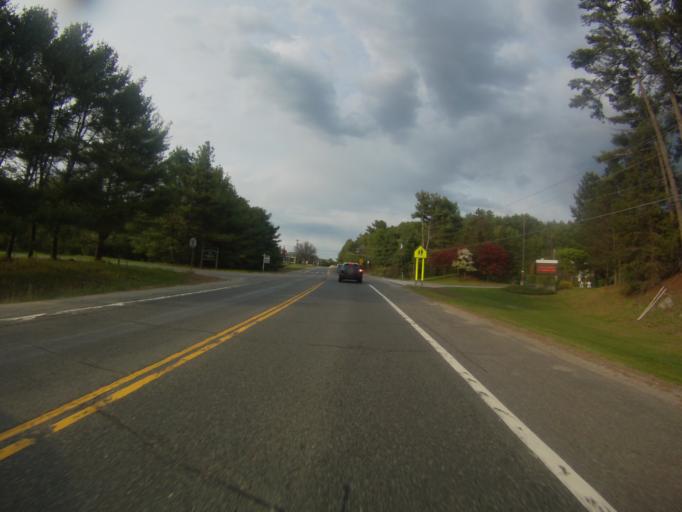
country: US
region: New York
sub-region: Warren County
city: Warrensburg
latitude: 43.6629
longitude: -73.7860
